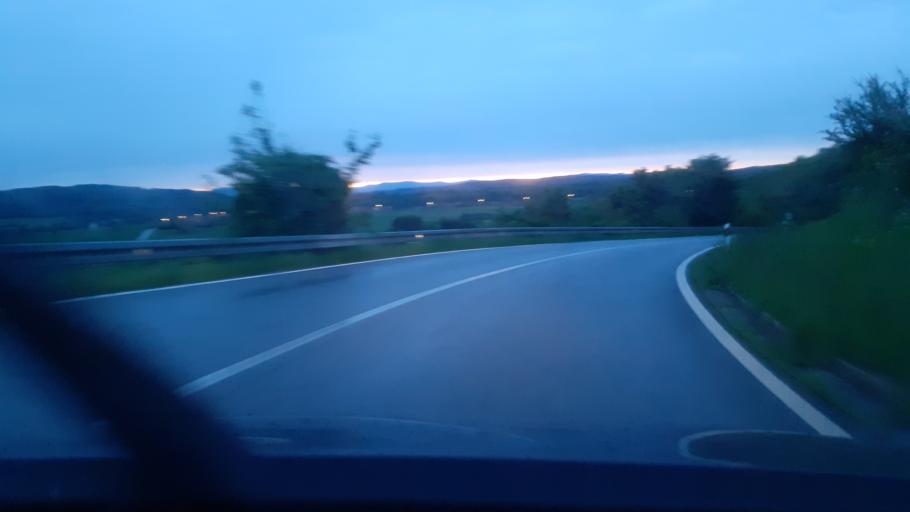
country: HR
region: Pozesko-Slavonska
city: Bilice
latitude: 45.2285
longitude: 17.8479
